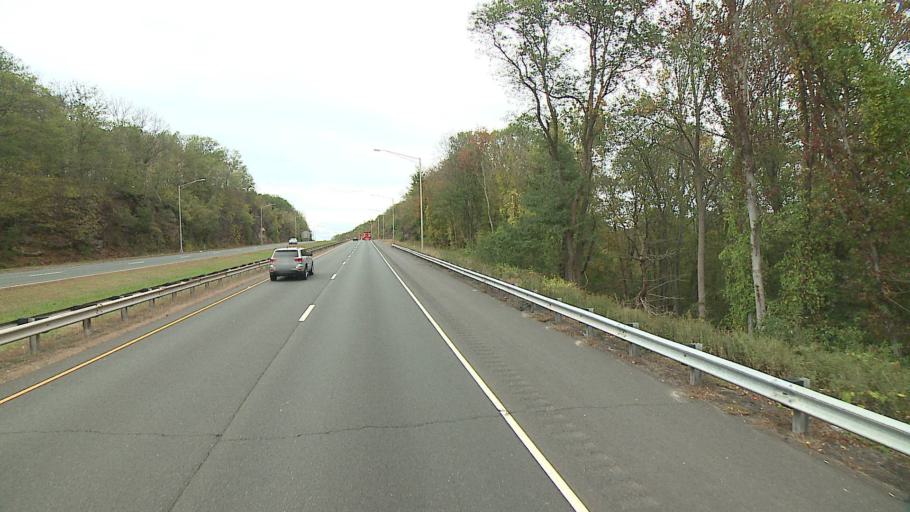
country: US
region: Connecticut
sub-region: Middlesex County
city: Higganum
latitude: 41.5204
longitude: -72.6049
